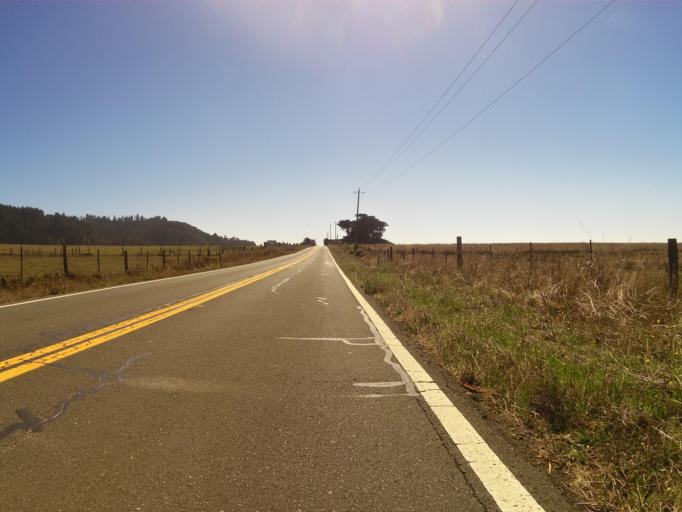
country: US
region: California
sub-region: Mendocino County
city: Boonville
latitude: 39.0452
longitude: -123.6842
